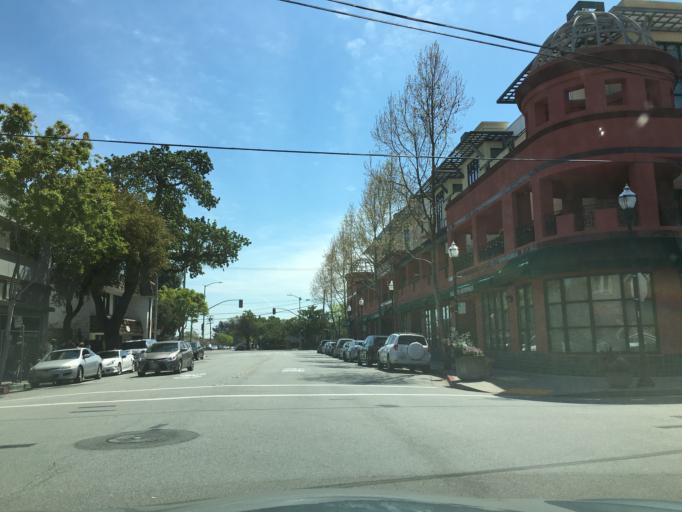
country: US
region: California
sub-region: San Mateo County
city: San Mateo
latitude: 37.5623
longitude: -122.3189
